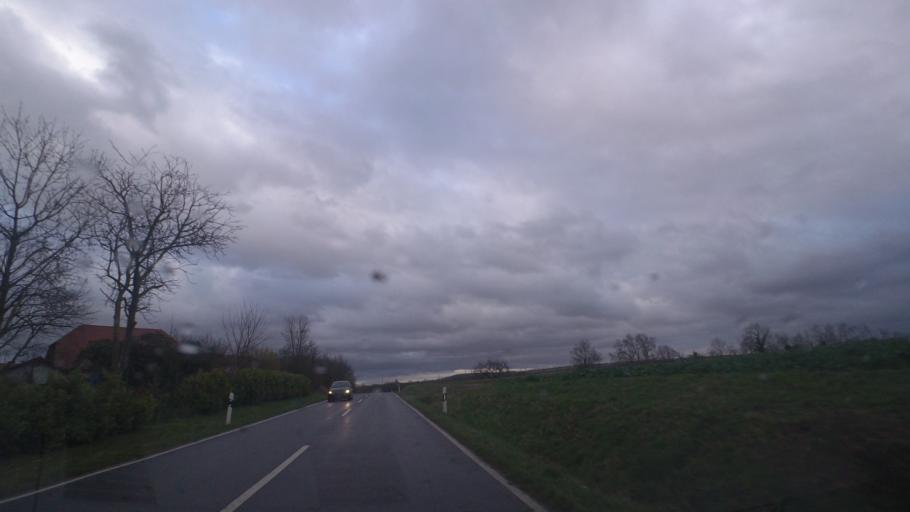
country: DE
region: Rheinland-Pfalz
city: Eppelsheim
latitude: 49.7018
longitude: 8.1696
